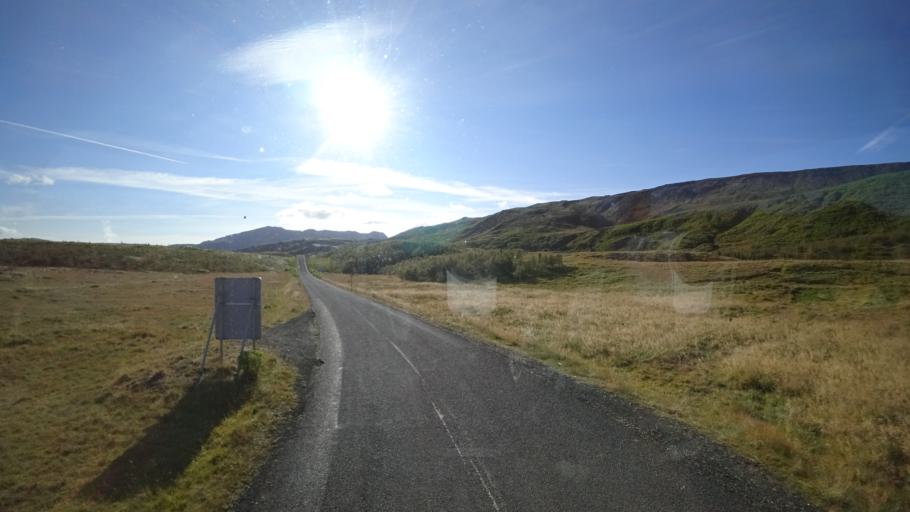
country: IS
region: South
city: Hveragerdi
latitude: 64.1253
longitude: -21.2503
